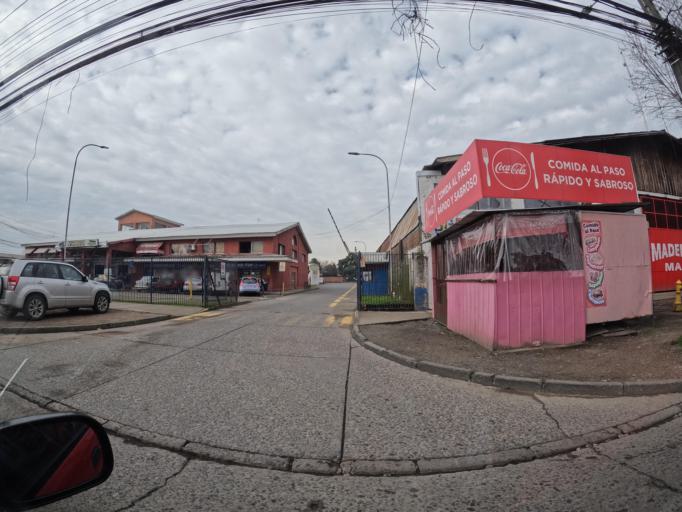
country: CL
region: Maule
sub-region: Provincia de Linares
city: Linares
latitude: -35.8473
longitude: -71.5896
